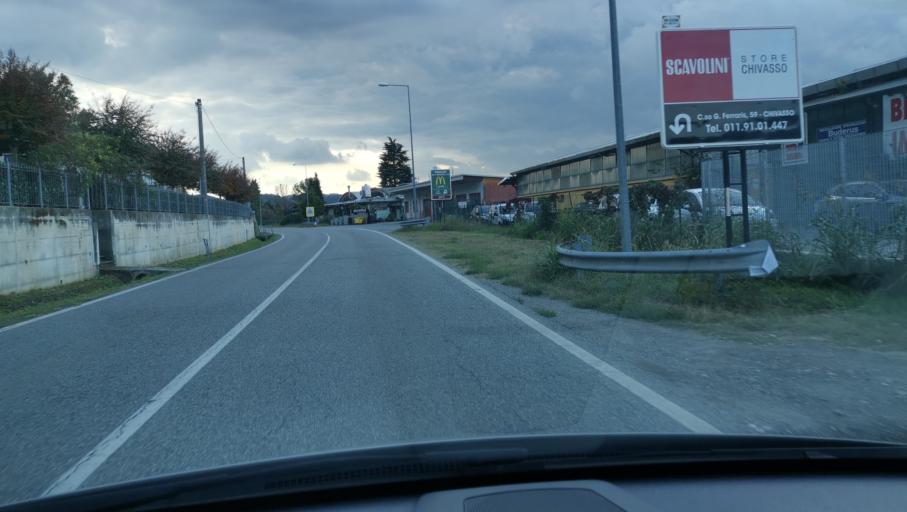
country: IT
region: Piedmont
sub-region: Provincia di Torino
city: Piana San Raffaele
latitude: 45.1596
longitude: 7.8532
